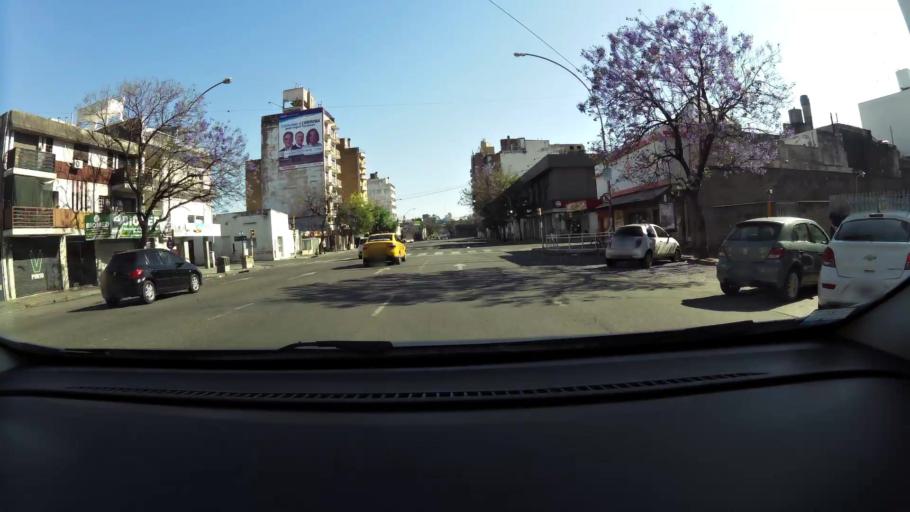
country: AR
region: Cordoba
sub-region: Departamento de Capital
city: Cordoba
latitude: -31.4128
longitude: -64.1782
